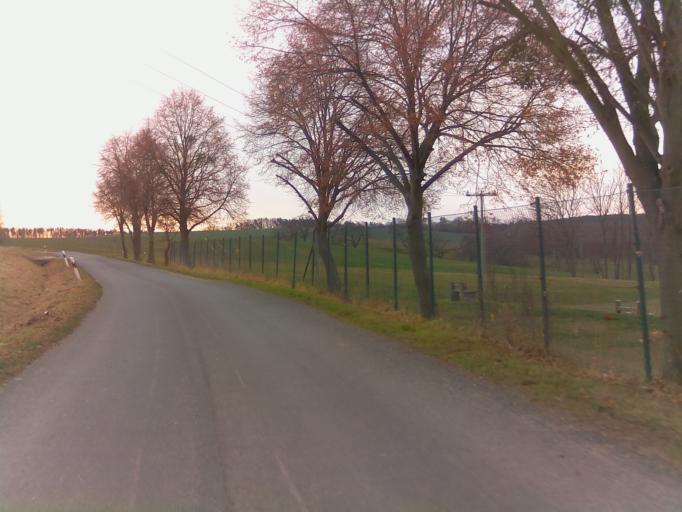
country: DE
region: Thuringia
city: Hundhaupten
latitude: 50.8334
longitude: 11.9949
